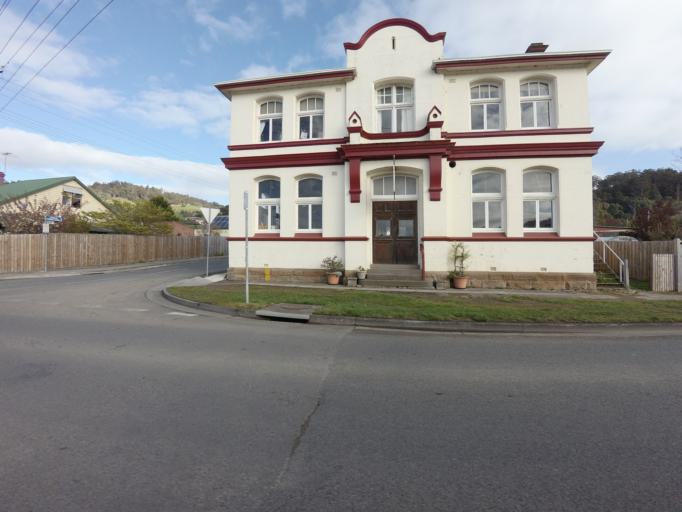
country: AU
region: Tasmania
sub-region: Huon Valley
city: Franklin
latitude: -43.0865
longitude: 147.0134
